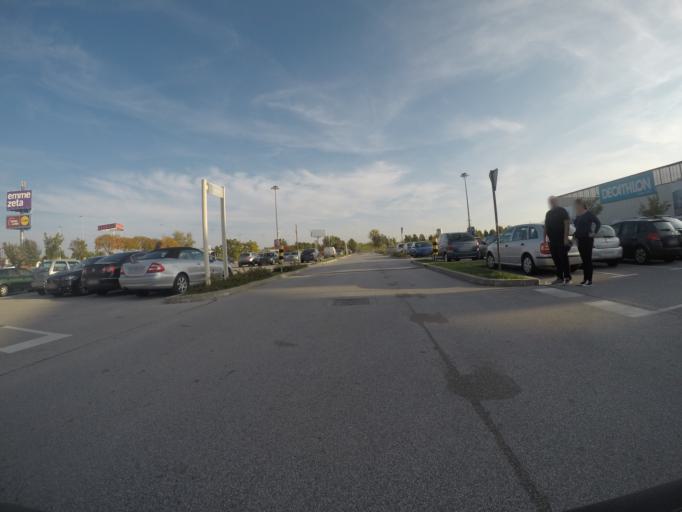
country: HR
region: Grad Zagreb
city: Jezdovec
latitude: 45.7964
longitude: 15.8576
